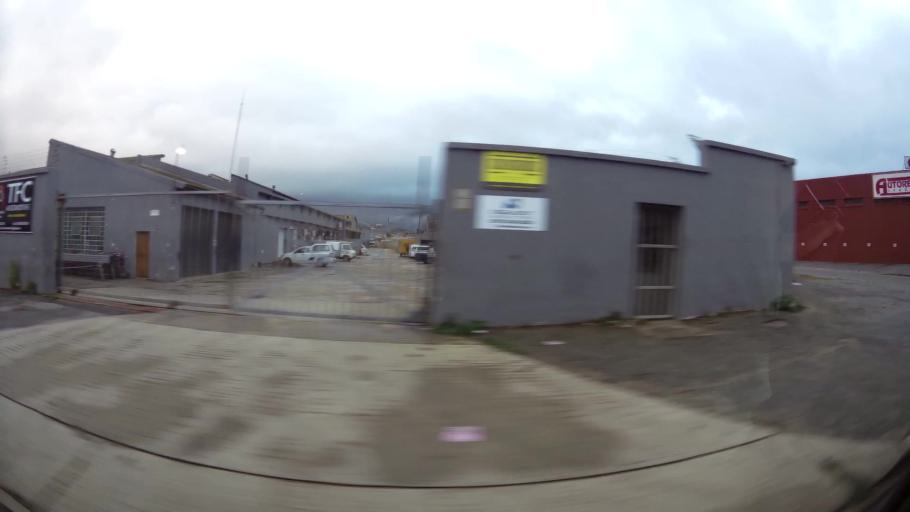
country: ZA
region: Eastern Cape
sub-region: Nelson Mandela Bay Metropolitan Municipality
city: Port Elizabeth
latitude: -33.9273
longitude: 25.5949
